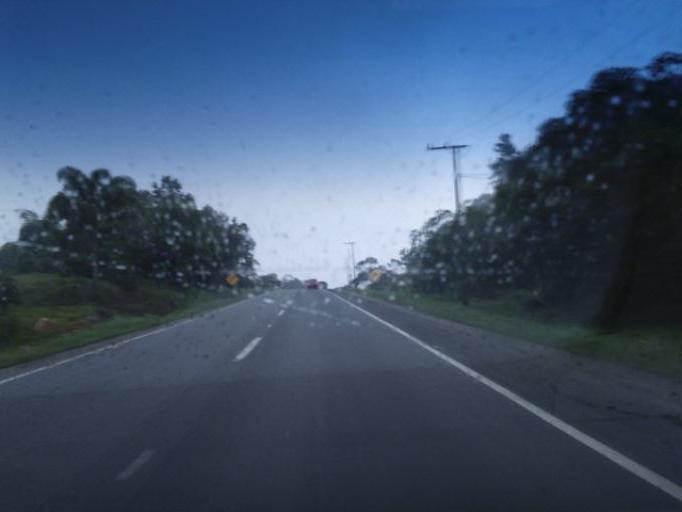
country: BR
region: Parana
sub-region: Guaratuba
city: Guaratuba
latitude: -25.9253
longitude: -48.9147
